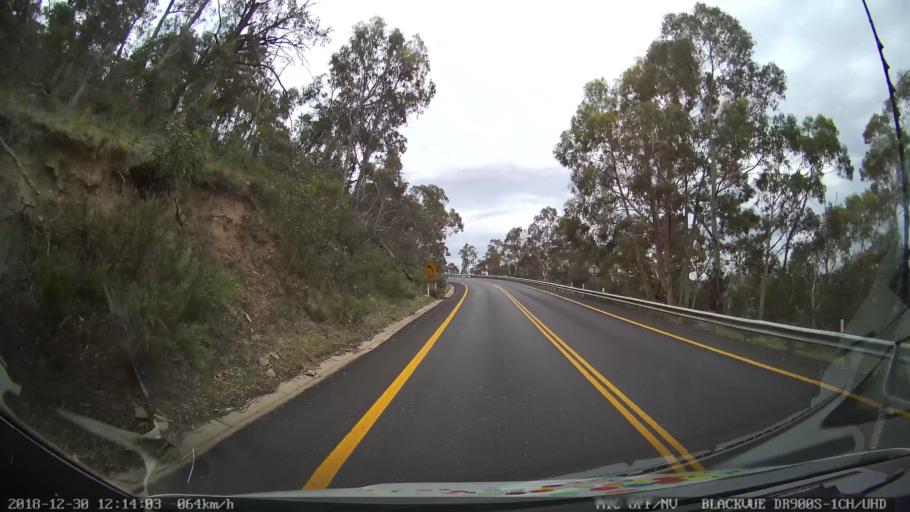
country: AU
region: New South Wales
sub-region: Snowy River
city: Jindabyne
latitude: -36.3461
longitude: 148.5803
